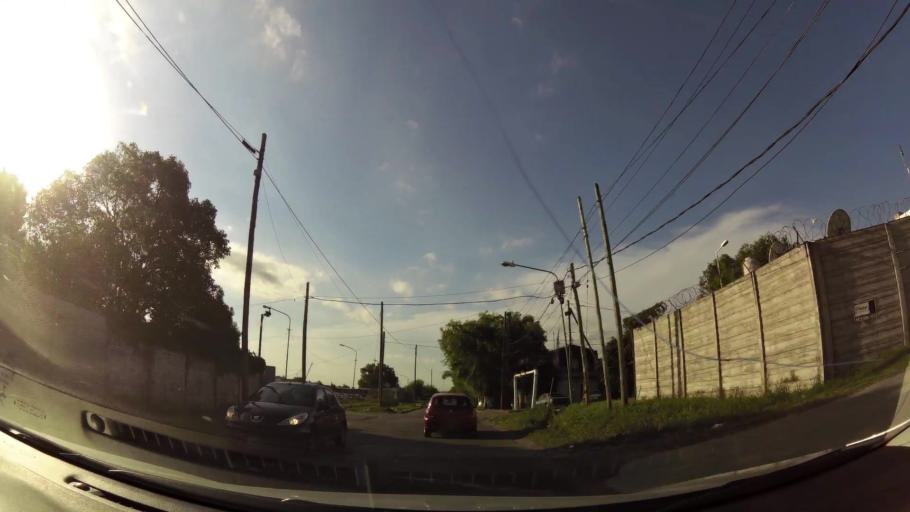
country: AR
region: Buenos Aires
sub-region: Partido de Tigre
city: Tigre
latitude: -34.4707
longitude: -58.6643
